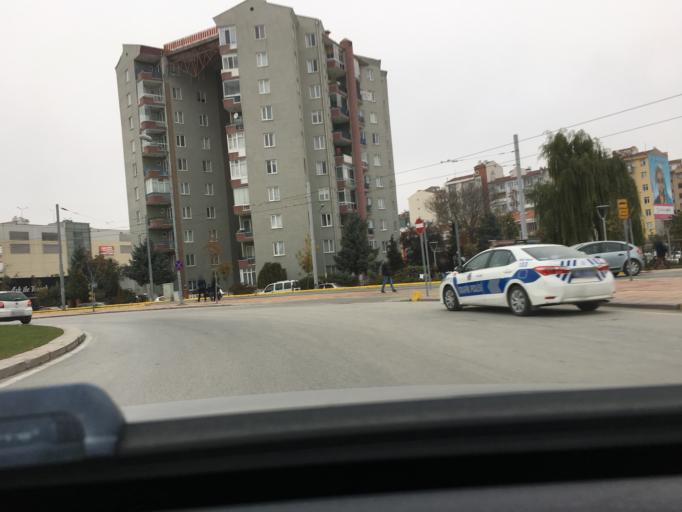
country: TR
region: Eskisehir
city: Eskisehir
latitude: 39.7805
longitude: 30.5117
